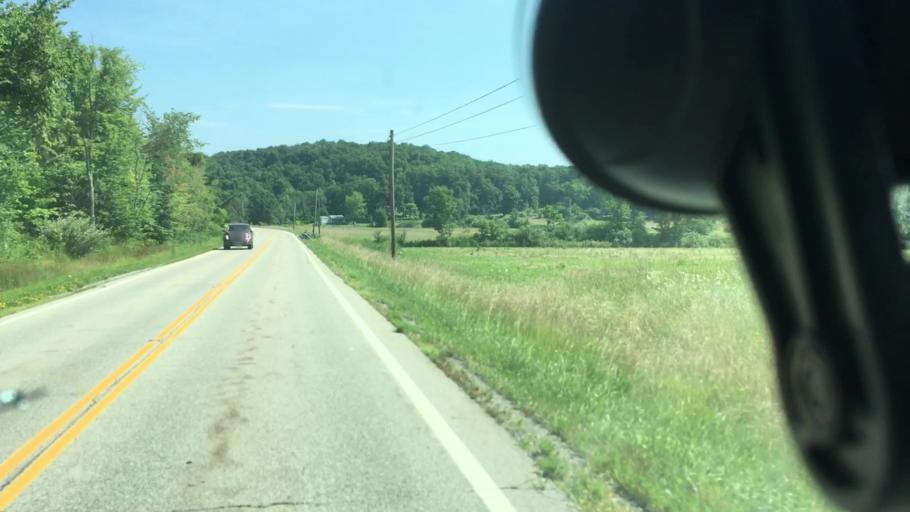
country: US
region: Ohio
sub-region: Columbiana County
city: Salineville
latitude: 40.6646
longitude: -80.8070
